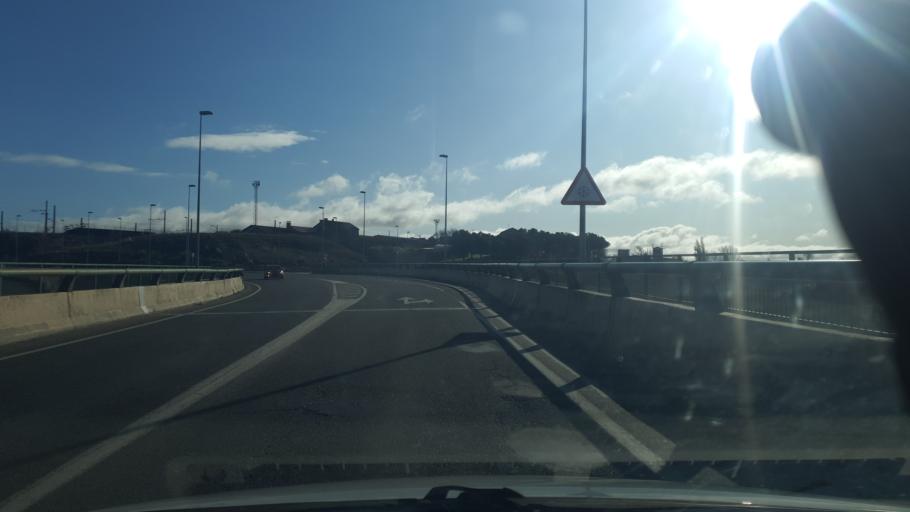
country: ES
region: Castille and Leon
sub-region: Provincia de Avila
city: Arevalo
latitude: 41.0495
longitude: -4.7056
